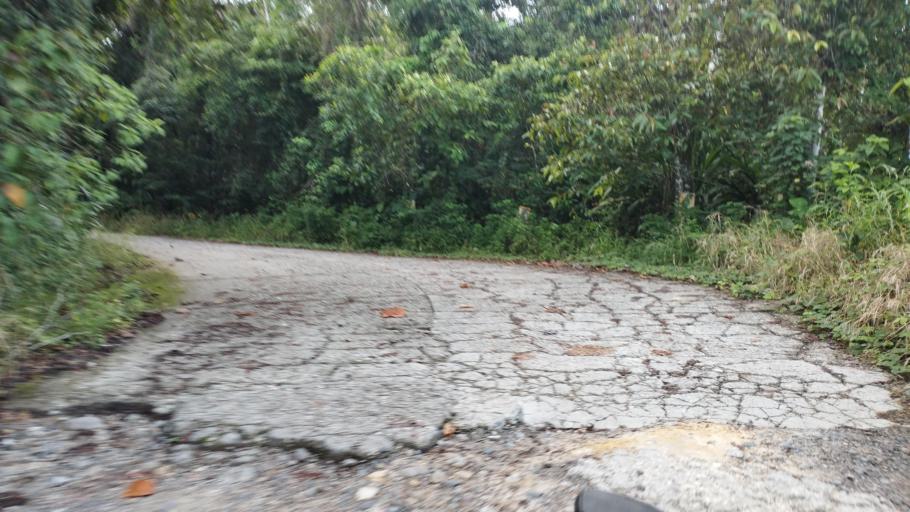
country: CO
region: Boyaca
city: San Luis de Gaceno
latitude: 4.8196
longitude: -73.1003
